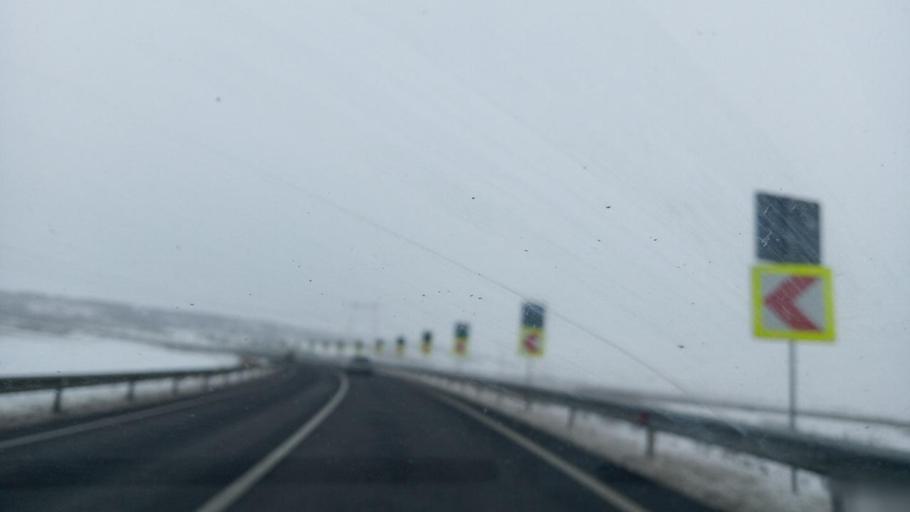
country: RO
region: Bacau
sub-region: Comuna Saucesti
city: Saucesti
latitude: 46.6377
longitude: 26.9308
